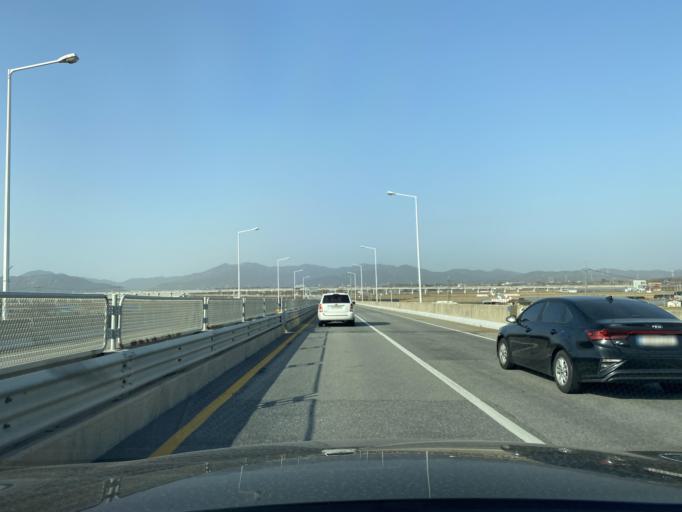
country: KR
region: Chungcheongnam-do
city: Yesan
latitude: 36.6914
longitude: 126.7365
